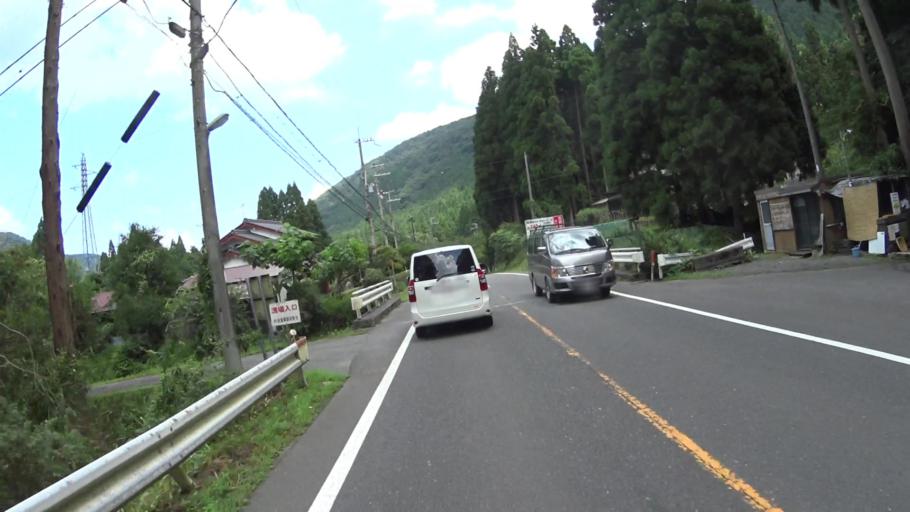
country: JP
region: Shiga Prefecture
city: Kitahama
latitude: 35.2916
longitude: 135.8837
